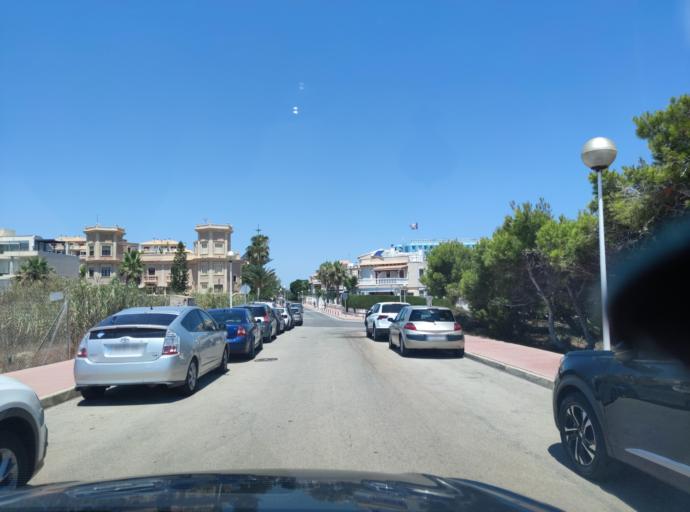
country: ES
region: Valencia
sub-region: Provincia de Alicante
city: Guardamar del Segura
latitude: 38.0634
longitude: -0.6526
